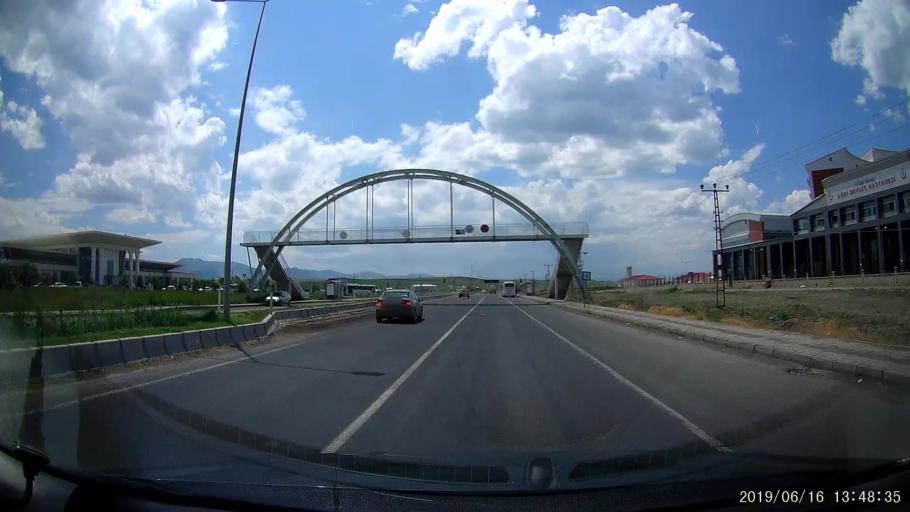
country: TR
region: Agri
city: Agri
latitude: 39.7146
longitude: 43.0043
